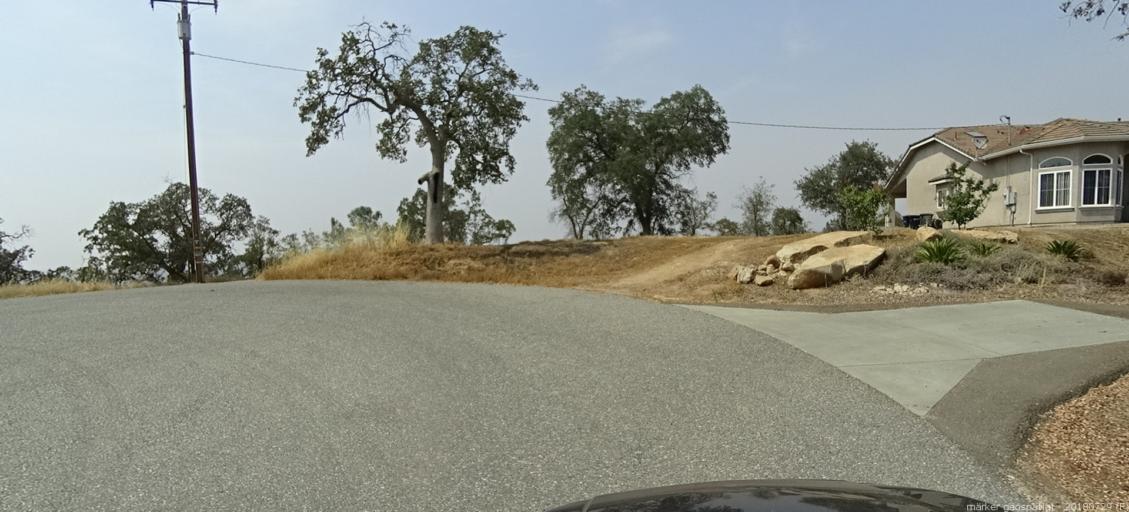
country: US
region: California
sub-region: Madera County
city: Yosemite Lakes
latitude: 37.2710
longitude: -119.8544
